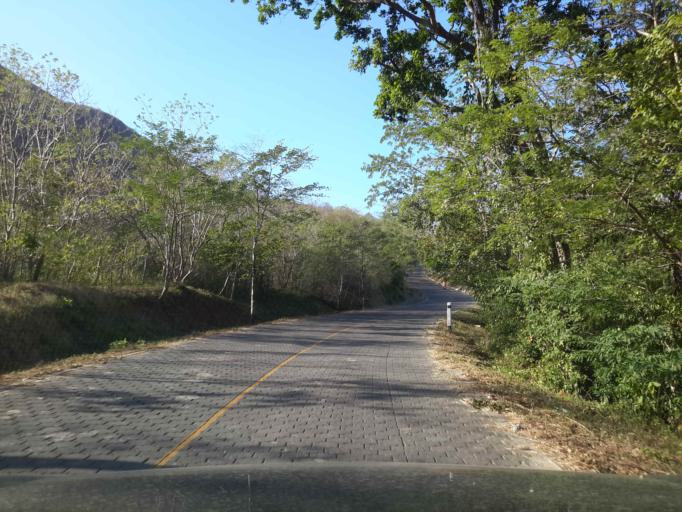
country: NI
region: Rivas
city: San Juan del Sur
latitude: 11.2303
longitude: -85.8259
